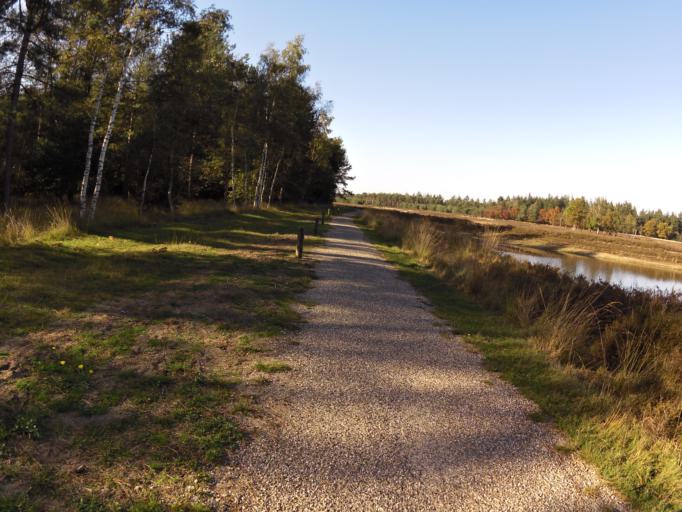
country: NL
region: North Brabant
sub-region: Gemeente Someren
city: Someren
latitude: 51.3695
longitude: 5.6565
